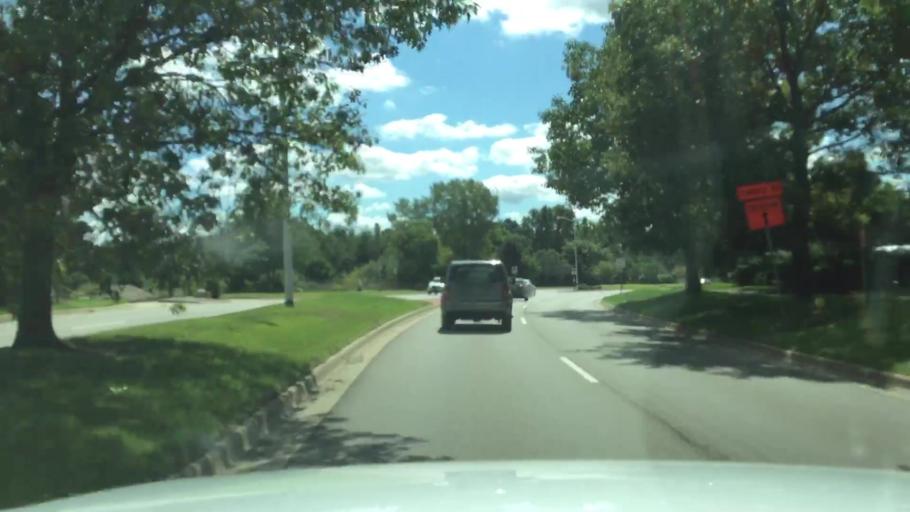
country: US
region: Michigan
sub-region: Kalamazoo County
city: Portage
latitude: 42.2229
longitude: -85.6010
